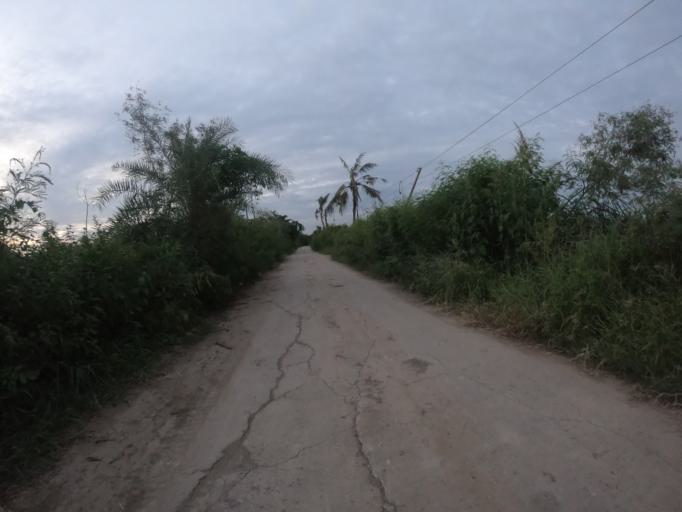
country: TH
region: Pathum Thani
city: Ban Lam Luk Ka
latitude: 14.0121
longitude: 100.8015
